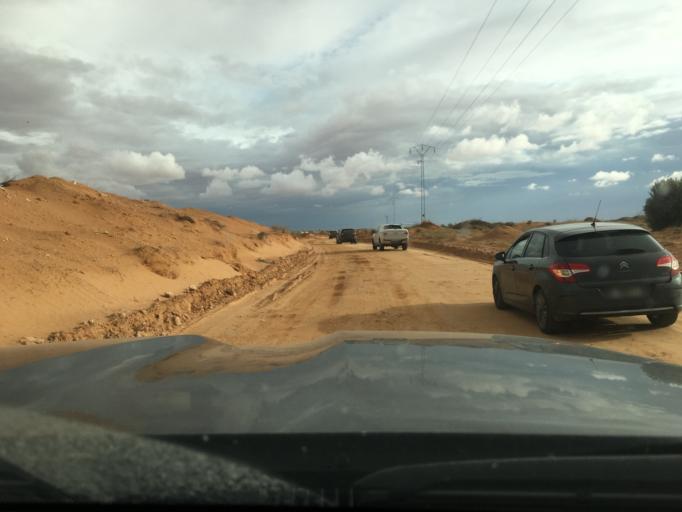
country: TN
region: Madanin
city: Medenine
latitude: 33.2711
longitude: 10.5672
